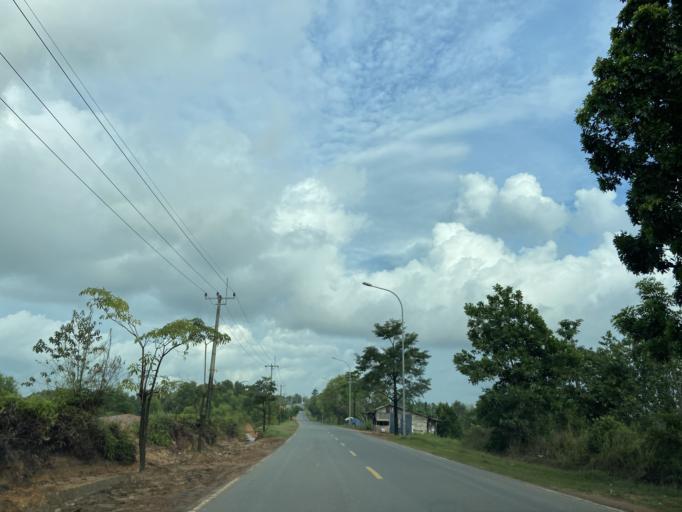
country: ID
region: Riau Islands
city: Tanjungpinang
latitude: 0.9378
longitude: 104.0920
